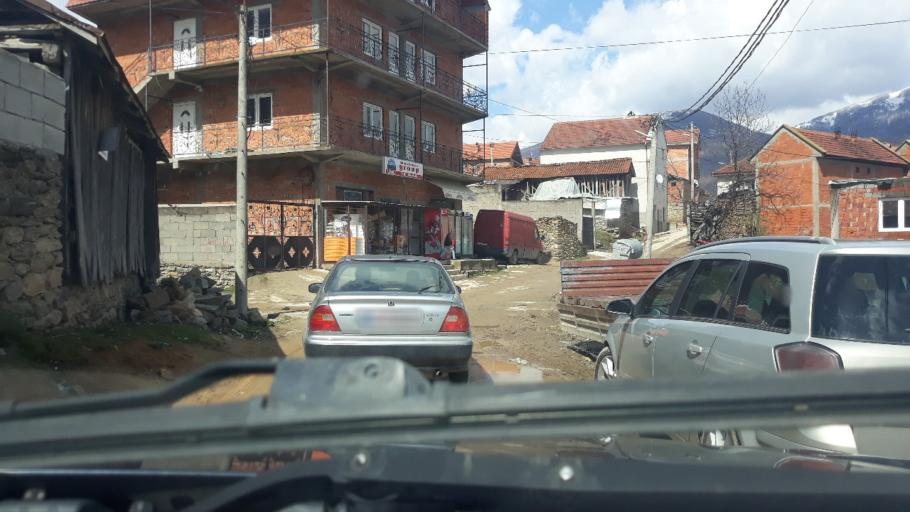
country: MK
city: Bogomila
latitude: 41.7218
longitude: 21.4854
